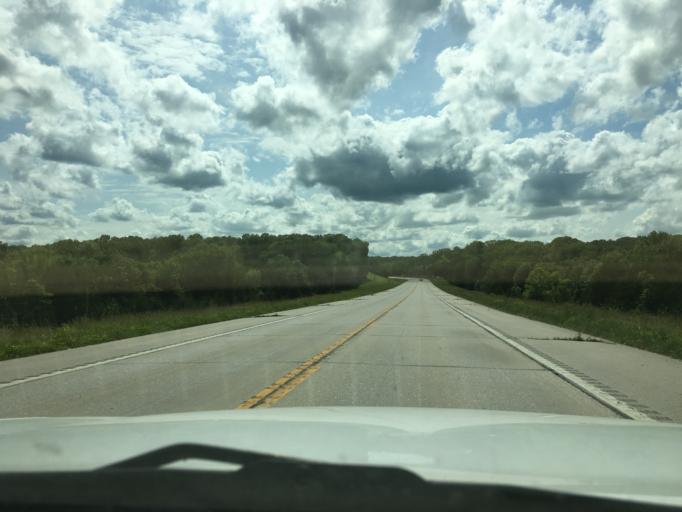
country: US
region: Missouri
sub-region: Franklin County
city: Gerald
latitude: 38.4235
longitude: -91.2732
